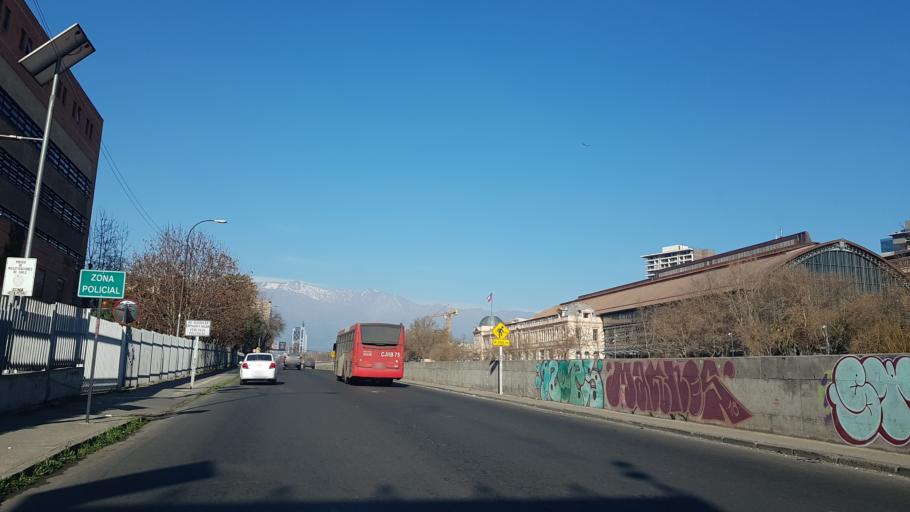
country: CL
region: Santiago Metropolitan
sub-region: Provincia de Santiago
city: Santiago
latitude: -33.4308
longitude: -70.6563
